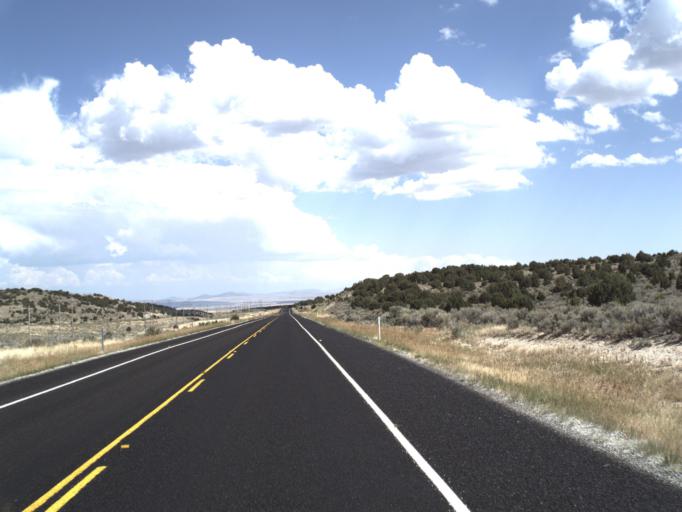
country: US
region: Idaho
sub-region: Minidoka County
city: Rupert
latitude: 41.9856
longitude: -113.1758
